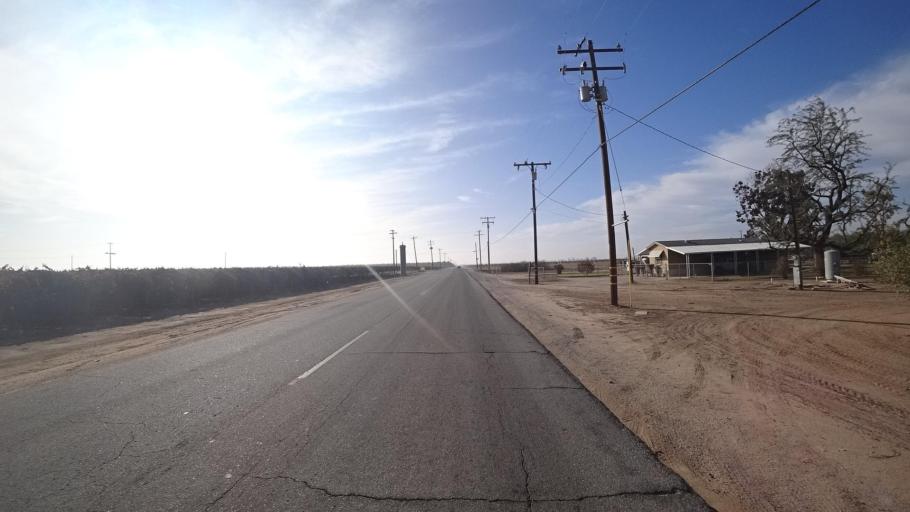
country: US
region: California
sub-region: Kern County
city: McFarland
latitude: 35.6612
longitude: -119.2047
